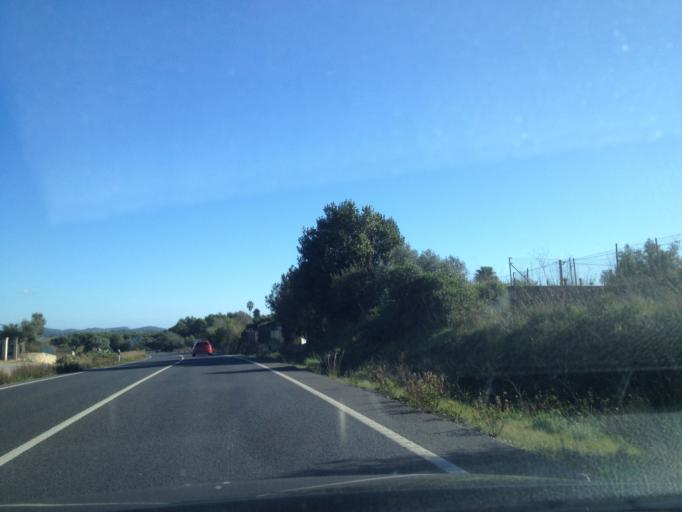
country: ES
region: Balearic Islands
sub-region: Illes Balears
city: Manacor
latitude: 39.5843
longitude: 3.2388
